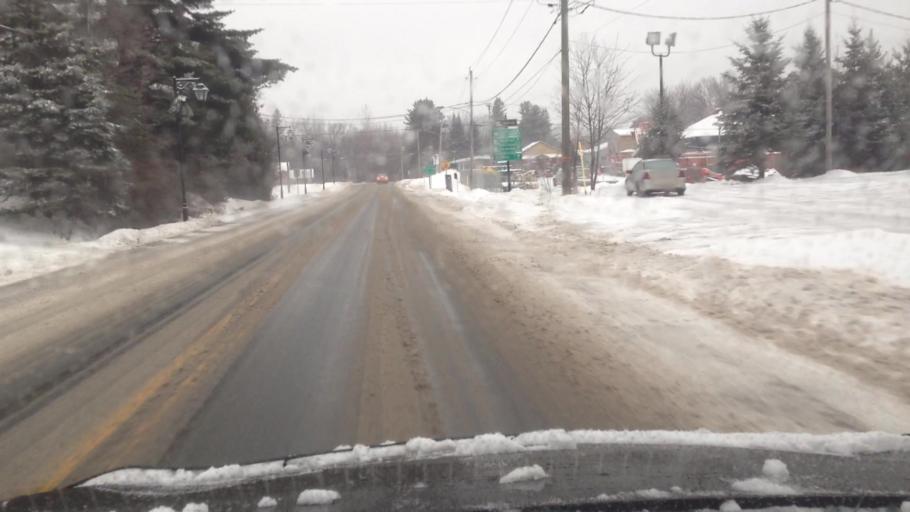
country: CA
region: Quebec
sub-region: Laurentides
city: Mont-Tremblant
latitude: 46.1170
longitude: -74.6053
